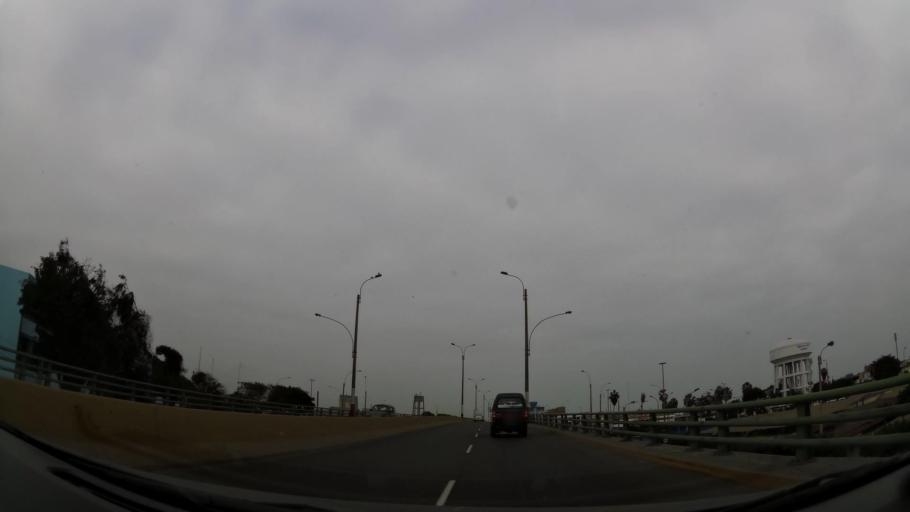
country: PE
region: Callao
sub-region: Callao
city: Callao
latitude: -12.0646
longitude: -77.1204
